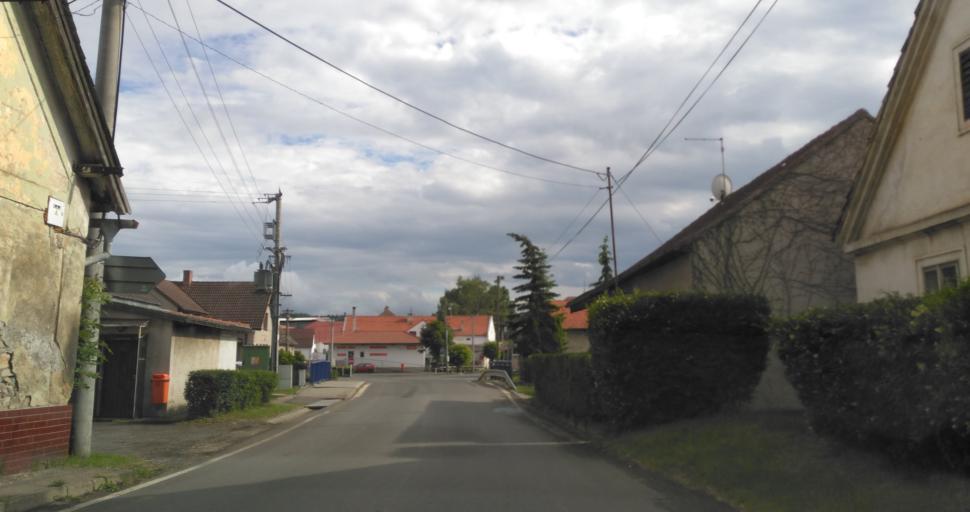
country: CZ
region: Central Bohemia
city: Hostomice
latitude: 49.8845
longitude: 14.0640
